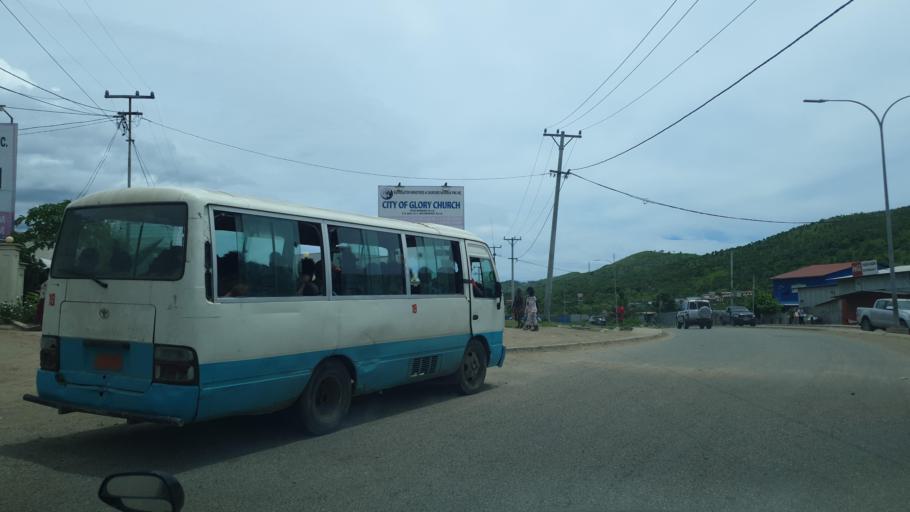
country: PG
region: National Capital
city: Port Moresby
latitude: -9.4822
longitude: 147.2126
